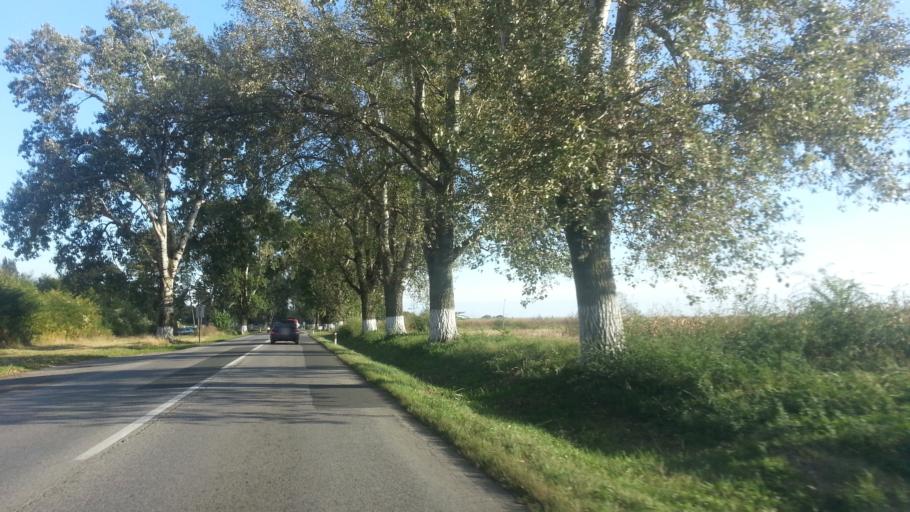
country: RS
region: Autonomna Pokrajina Vojvodina
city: Nova Pazova
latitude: 44.9282
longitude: 20.2427
